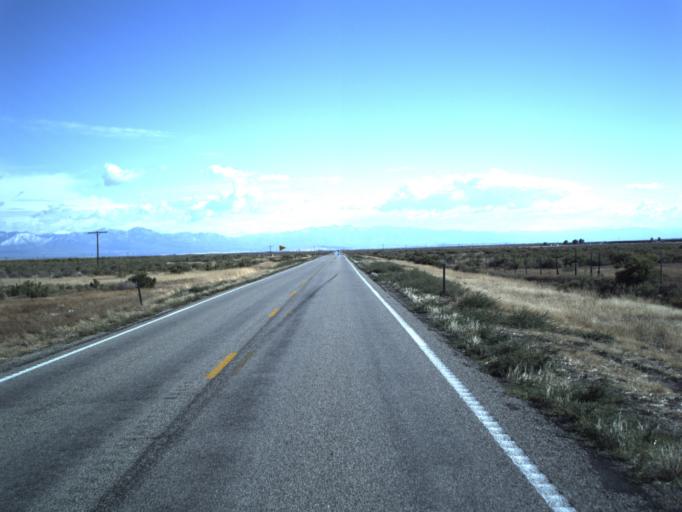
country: US
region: Utah
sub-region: Millard County
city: Delta
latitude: 39.3314
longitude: -112.4875
